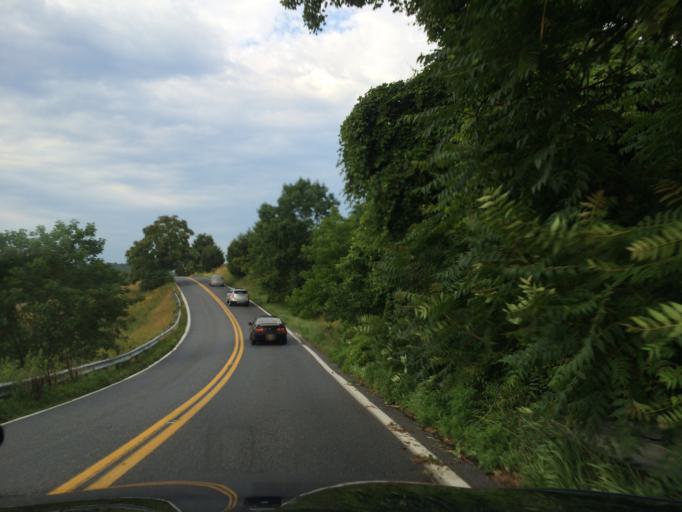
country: US
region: Maryland
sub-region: Frederick County
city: Green Valley
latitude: 39.2805
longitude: -77.2747
